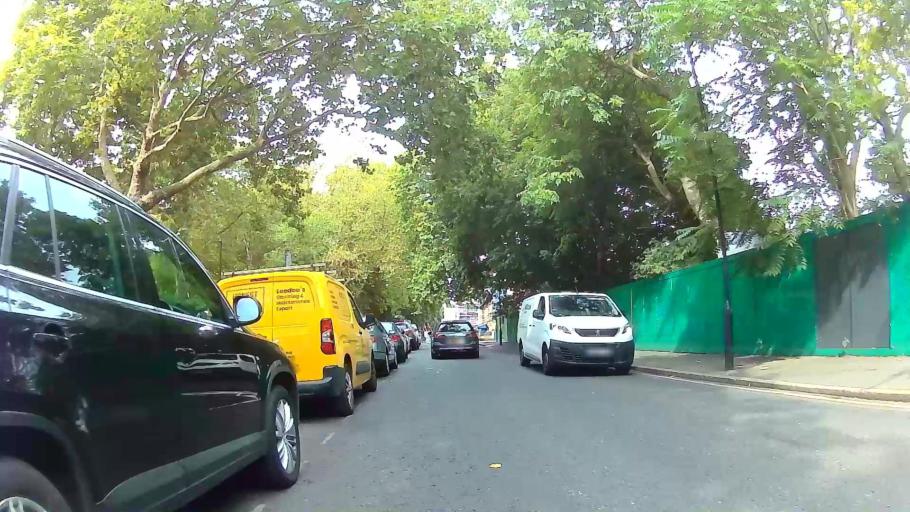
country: GB
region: England
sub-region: Greater London
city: Hackney
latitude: 51.5555
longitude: -0.0639
